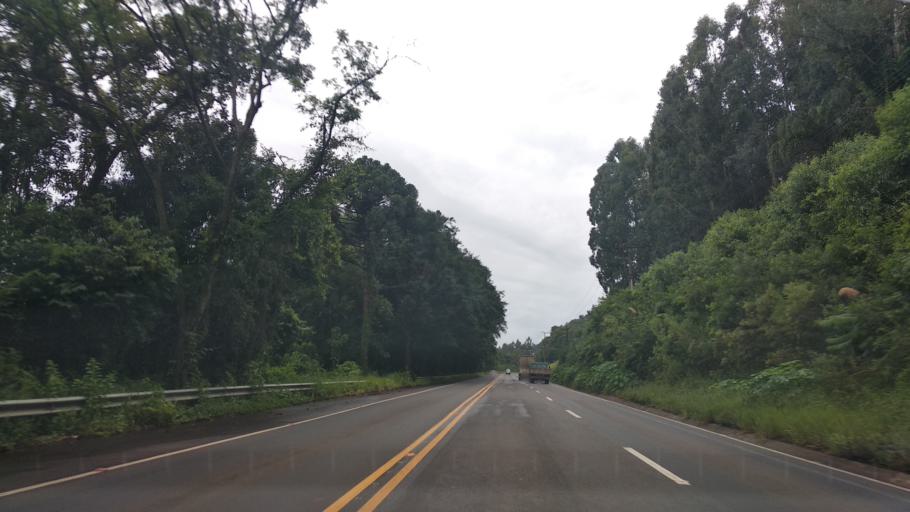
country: BR
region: Santa Catarina
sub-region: Videira
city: Videira
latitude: -27.0685
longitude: -51.2366
